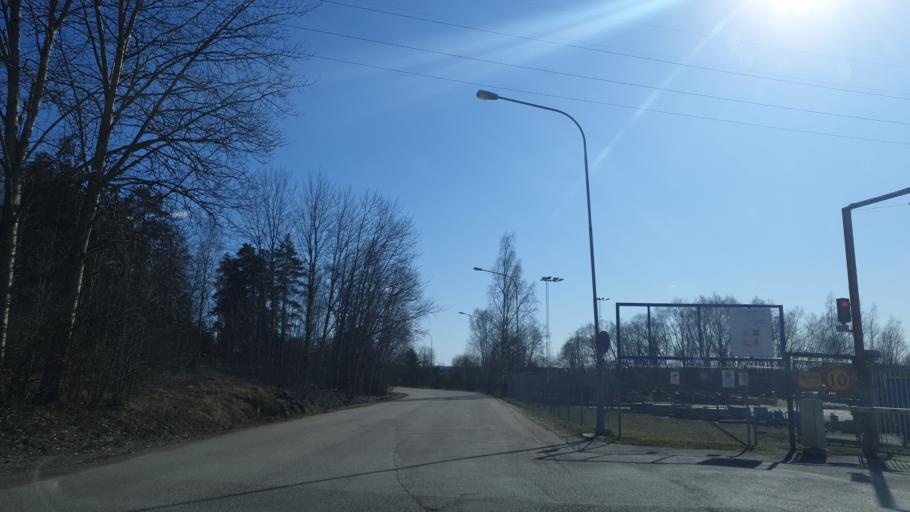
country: SE
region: Vaestmanland
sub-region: Kopings Kommun
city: Koping
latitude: 59.4975
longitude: 16.0398
